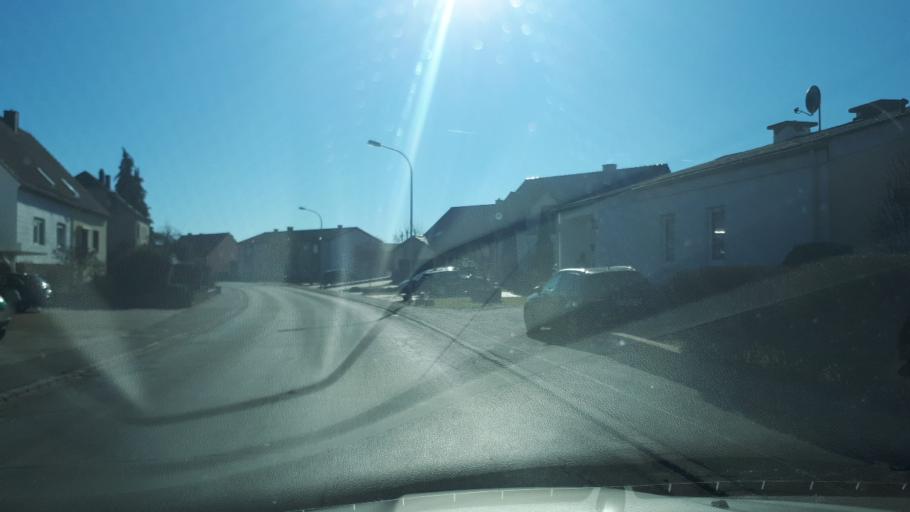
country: DE
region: Rheinland-Pfalz
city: Saxler
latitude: 50.1262
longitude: 6.9057
